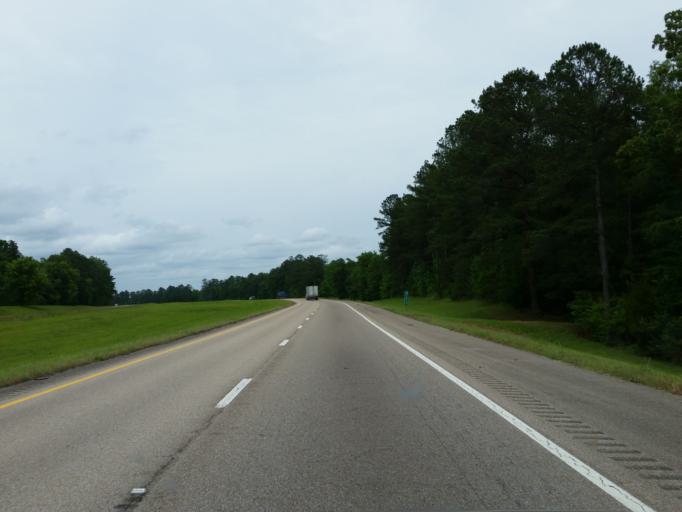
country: US
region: Mississippi
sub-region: Clarke County
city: Stonewall
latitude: 32.0127
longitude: -88.9268
